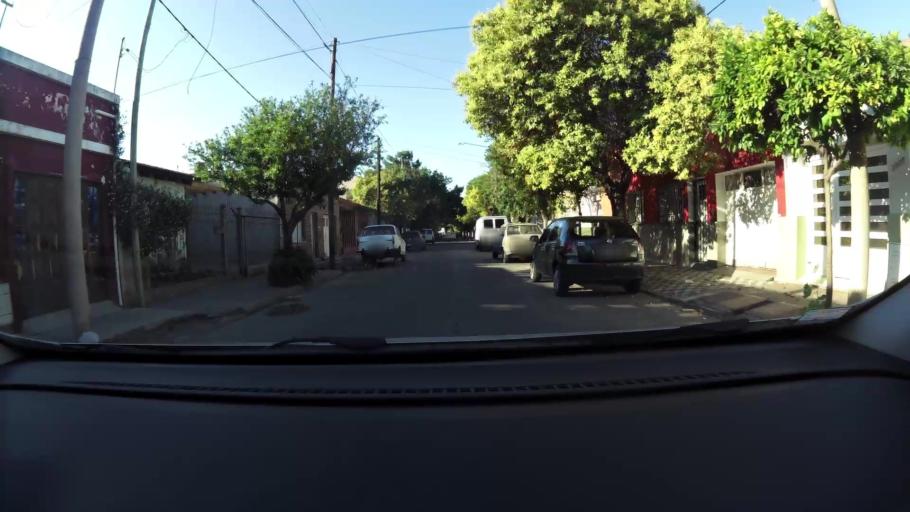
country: AR
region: Cordoba
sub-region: Departamento de Capital
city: Cordoba
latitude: -31.3833
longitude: -64.1922
